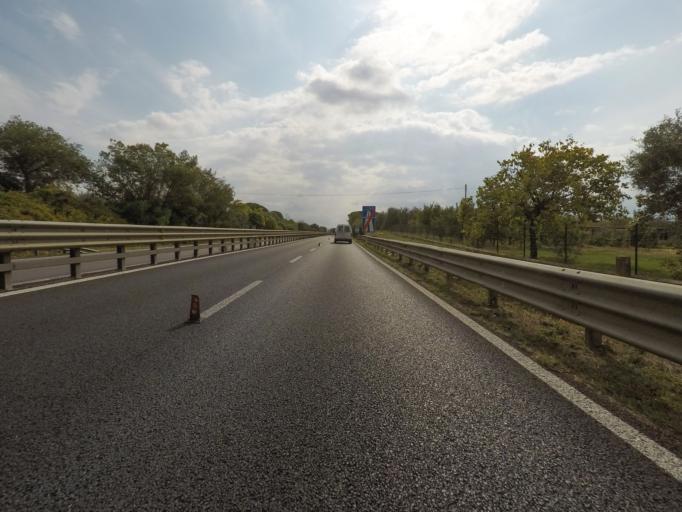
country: IT
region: Tuscany
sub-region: Provincia di Grosseto
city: Grosseto
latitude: 42.7257
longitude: 11.1370
